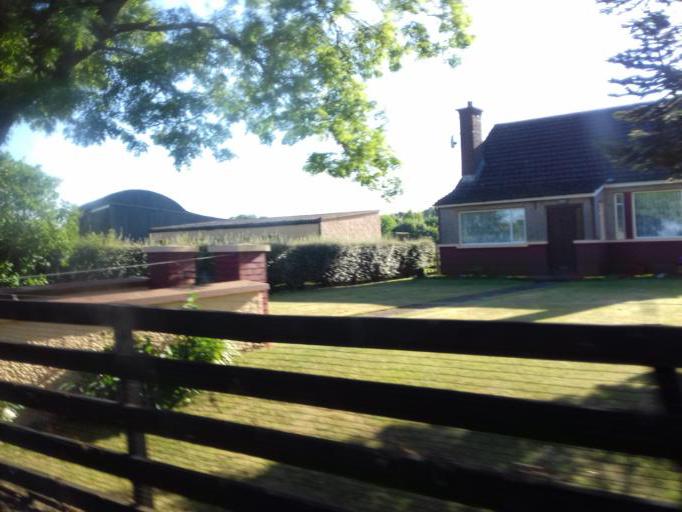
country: IE
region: Leinster
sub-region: Dublin City
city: Finglas
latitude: 53.4340
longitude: -6.3277
